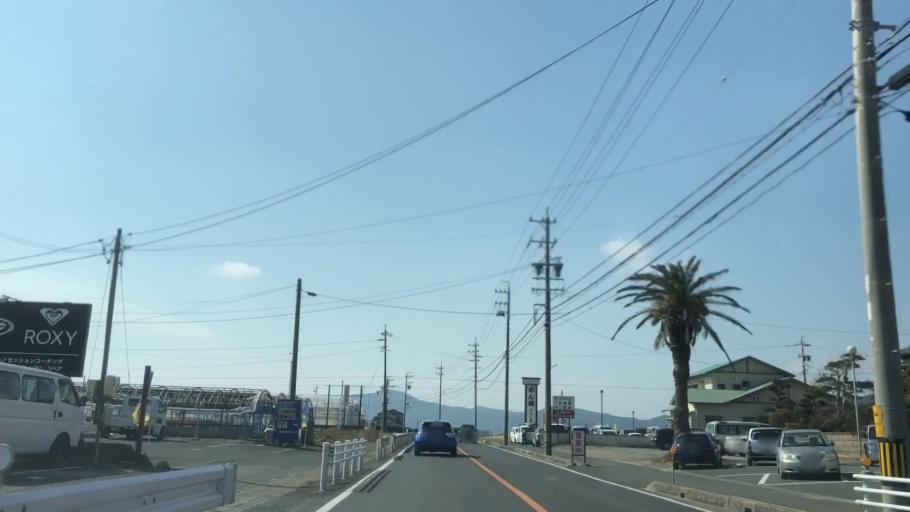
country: JP
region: Aichi
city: Tahara
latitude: 34.6178
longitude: 137.2117
